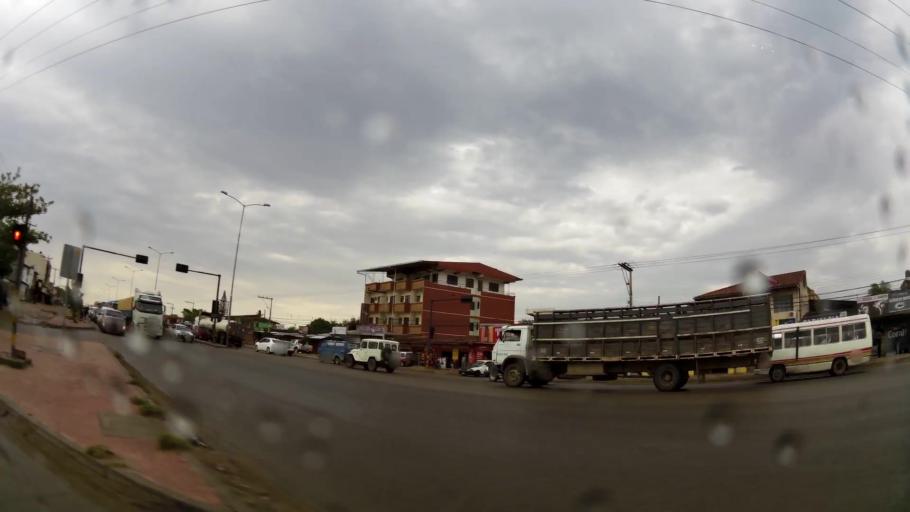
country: BO
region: Santa Cruz
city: Santa Cruz de la Sierra
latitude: -17.7675
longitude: -63.1157
